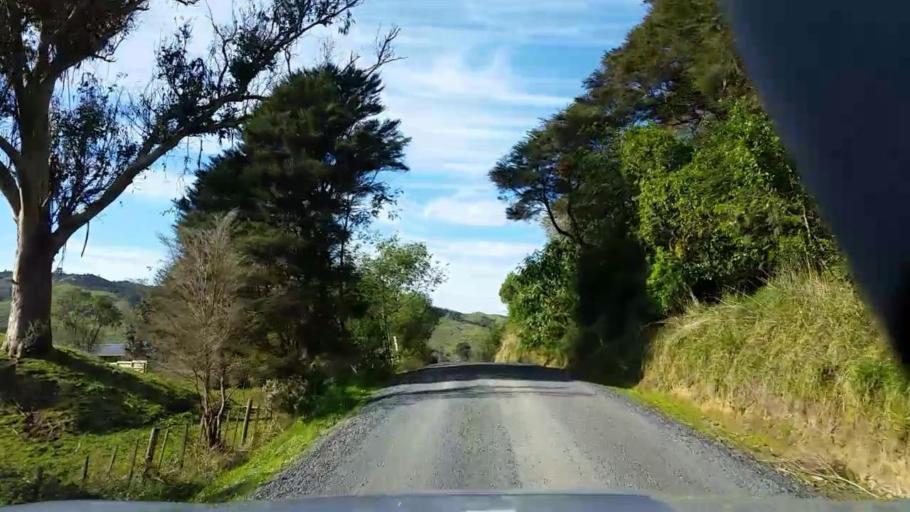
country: NZ
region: Waikato
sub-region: Hauraki District
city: Ngatea
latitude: -37.4769
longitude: 175.4060
